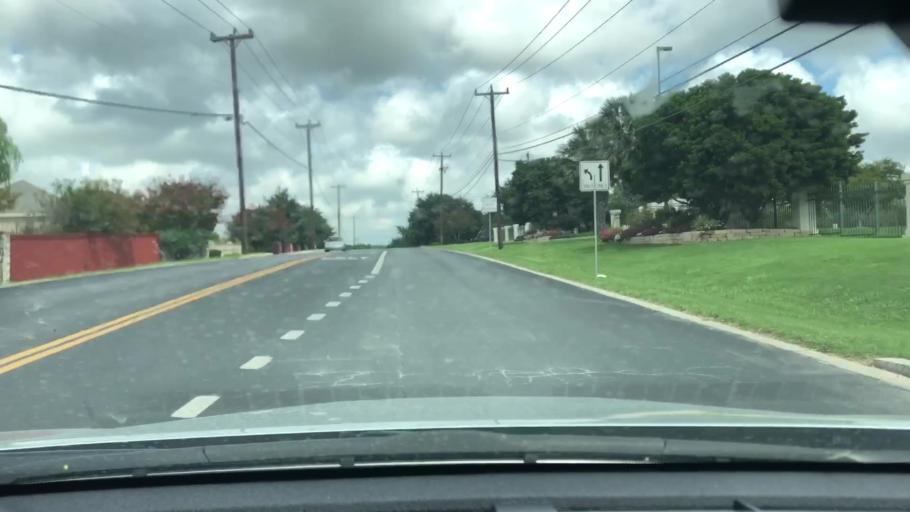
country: US
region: Texas
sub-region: Bexar County
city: Windcrest
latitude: 29.5274
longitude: -98.3693
